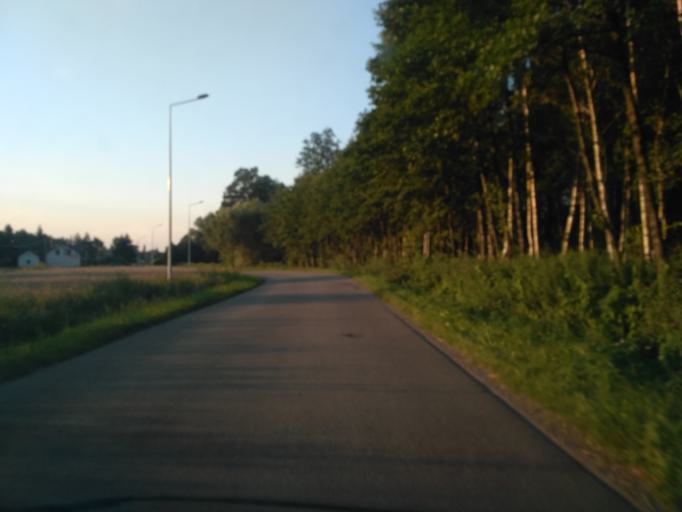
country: PL
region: Subcarpathian Voivodeship
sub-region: Powiat strzyzowski
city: Wysoka Strzyzowska
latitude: 49.8195
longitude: 21.7417
